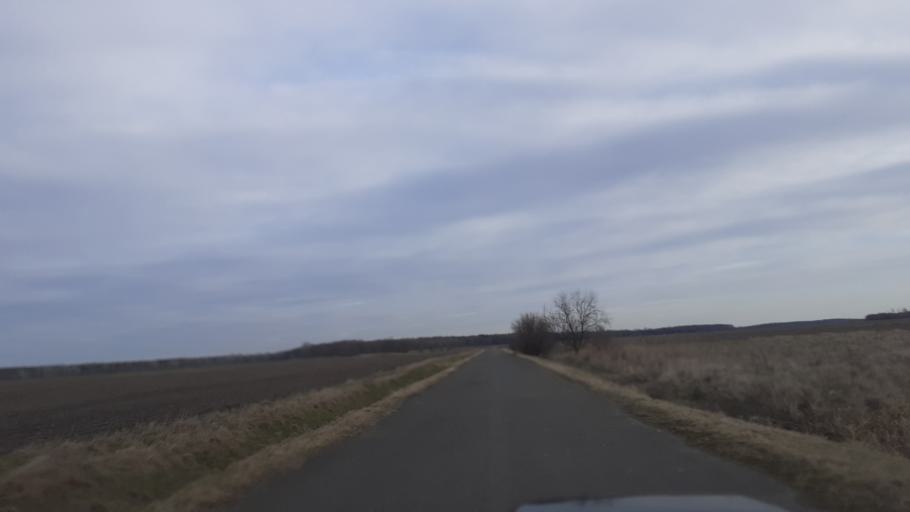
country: HU
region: Fejer
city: Szabadbattyan
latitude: 47.1057
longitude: 18.4399
